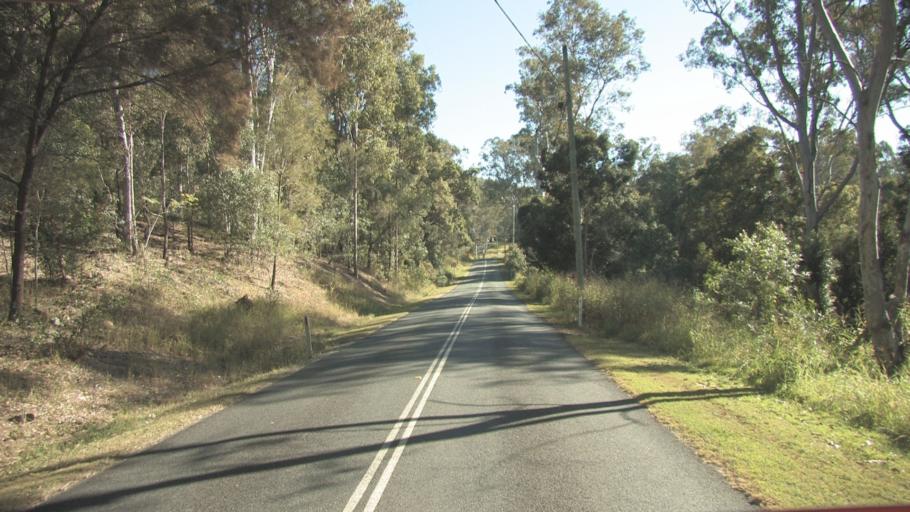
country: AU
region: Queensland
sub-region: Logan
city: Windaroo
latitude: -27.8056
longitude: 153.1697
